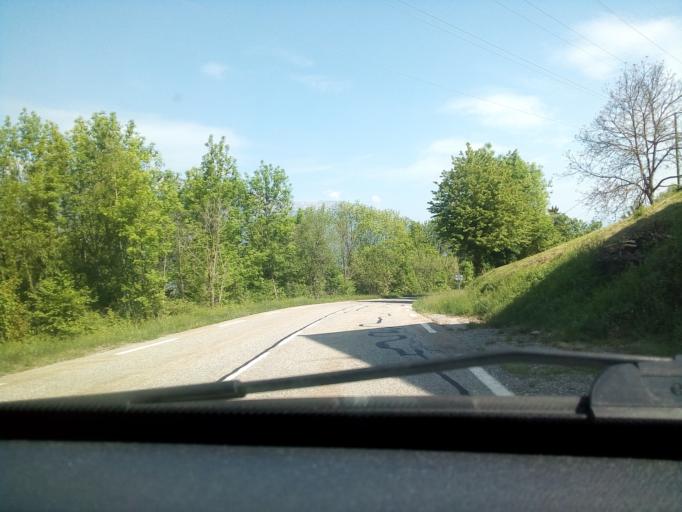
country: FR
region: Rhone-Alpes
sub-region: Departement de l'Isere
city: Le Champ-pres-Froges
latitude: 45.2728
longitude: 5.9393
